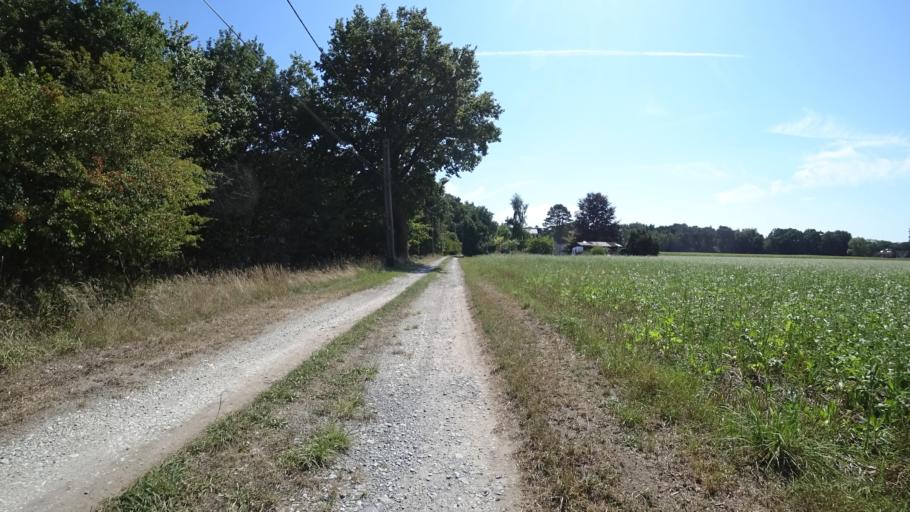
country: DE
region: North Rhine-Westphalia
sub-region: Regierungsbezirk Detmold
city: Verl
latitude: 51.9490
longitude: 8.4695
